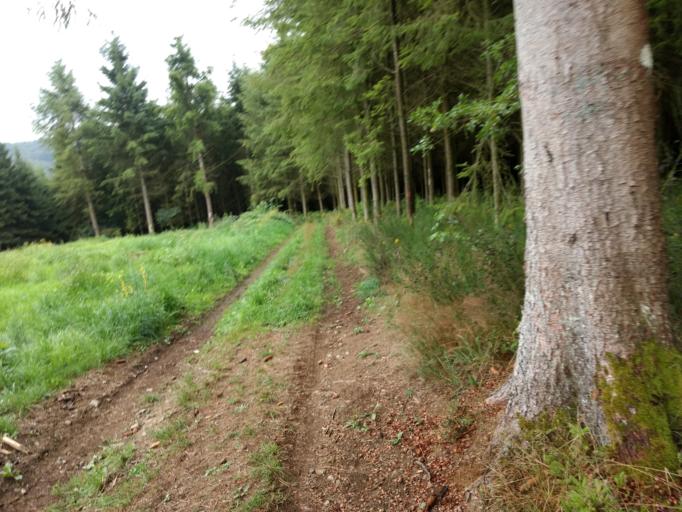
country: BE
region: Wallonia
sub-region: Province du Luxembourg
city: Bertogne
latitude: 50.1377
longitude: 5.7073
